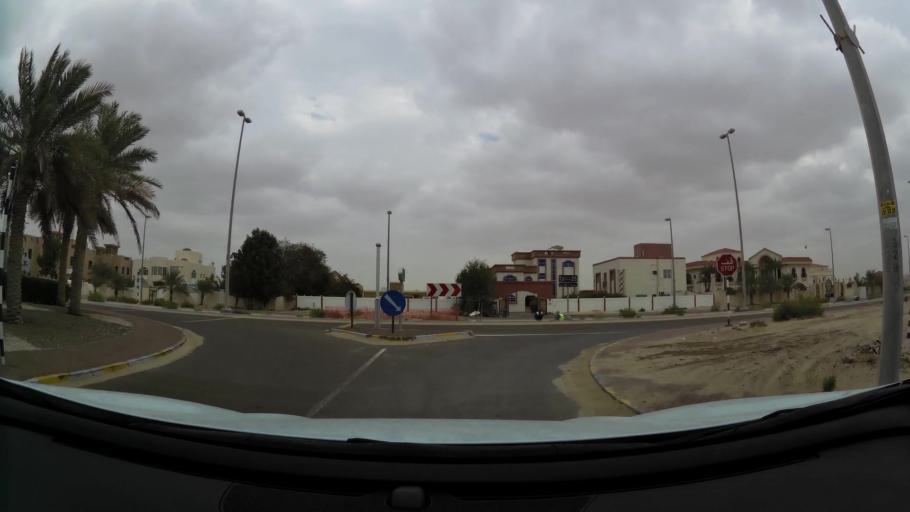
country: AE
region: Abu Dhabi
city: Abu Dhabi
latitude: 24.3722
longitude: 54.6406
